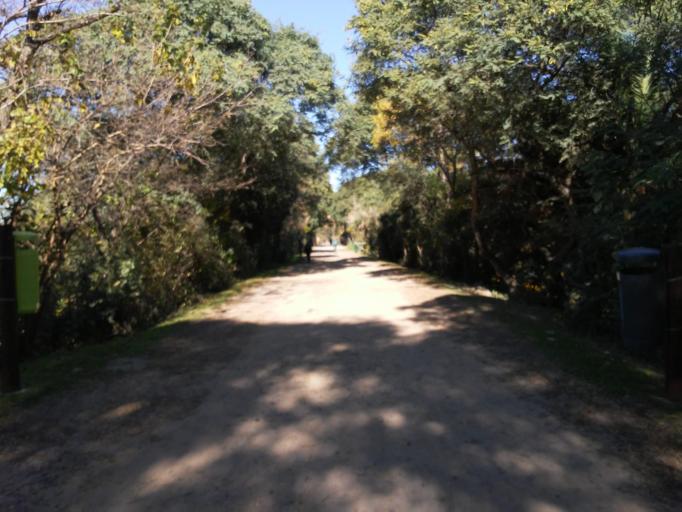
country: AR
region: Buenos Aires F.D.
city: Buenos Aires
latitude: -34.6148
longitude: -58.3556
